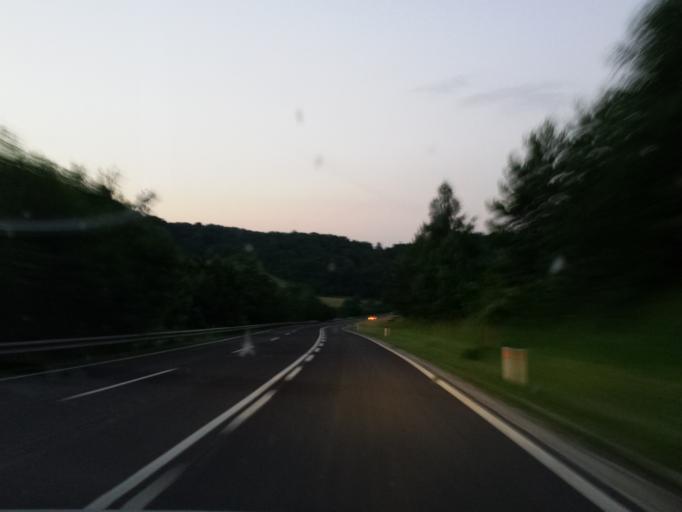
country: AT
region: Lower Austria
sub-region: Politischer Bezirk Baden
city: Alland
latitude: 48.0427
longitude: 16.0435
